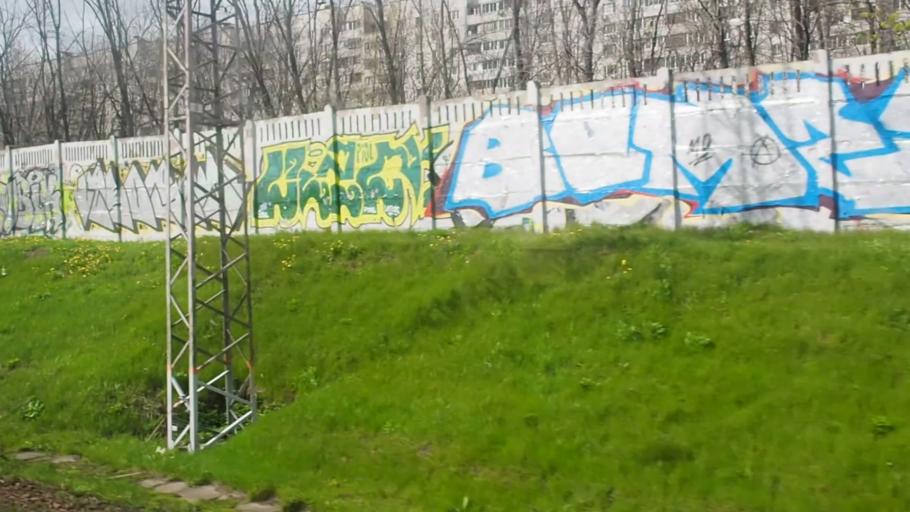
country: RU
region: Moskovskaya
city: Bol'shaya Setun'
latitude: 55.7269
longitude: 37.4232
